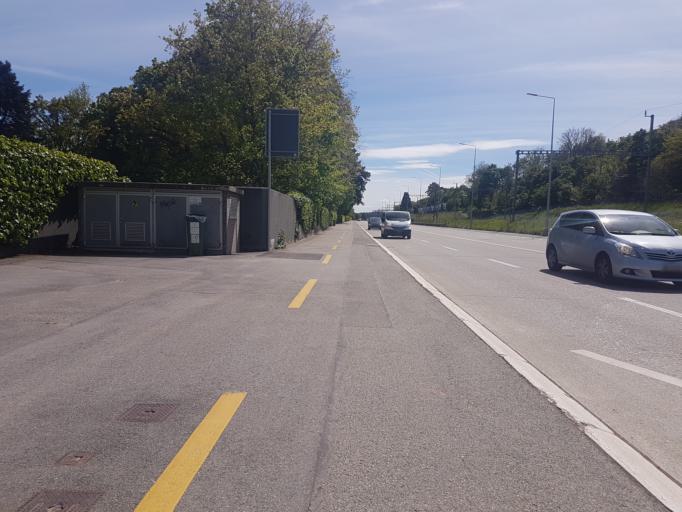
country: CH
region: Geneva
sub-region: Geneva
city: Versoix
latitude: 46.2702
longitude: 6.1655
